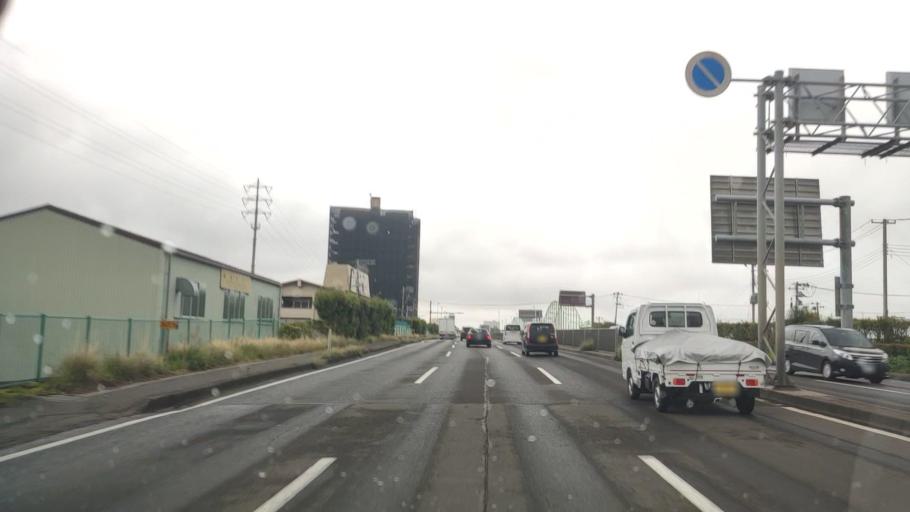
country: JP
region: Miyagi
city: Sendai
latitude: 38.2230
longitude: 140.8989
